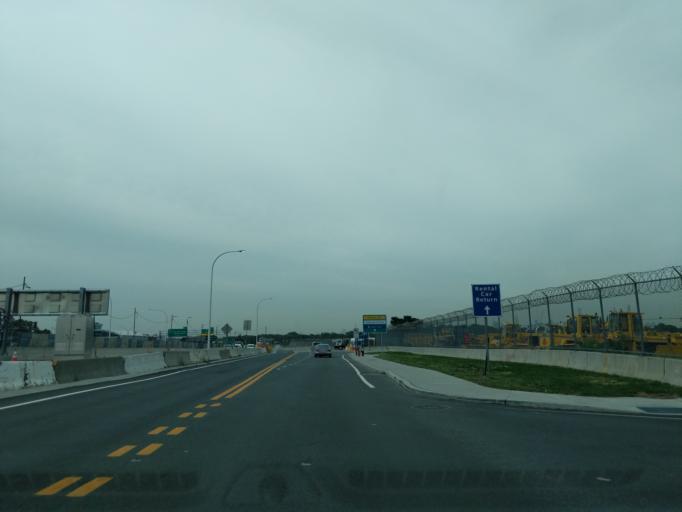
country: US
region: New York
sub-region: Queens County
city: Long Island City
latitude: 40.7715
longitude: -73.8787
